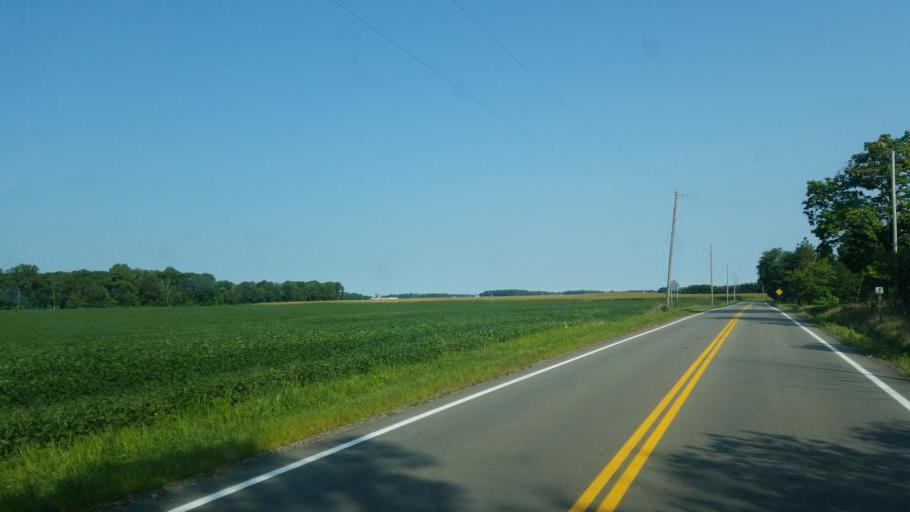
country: US
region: Ohio
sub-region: Richland County
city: Shelby
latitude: 40.8084
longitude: -82.6565
